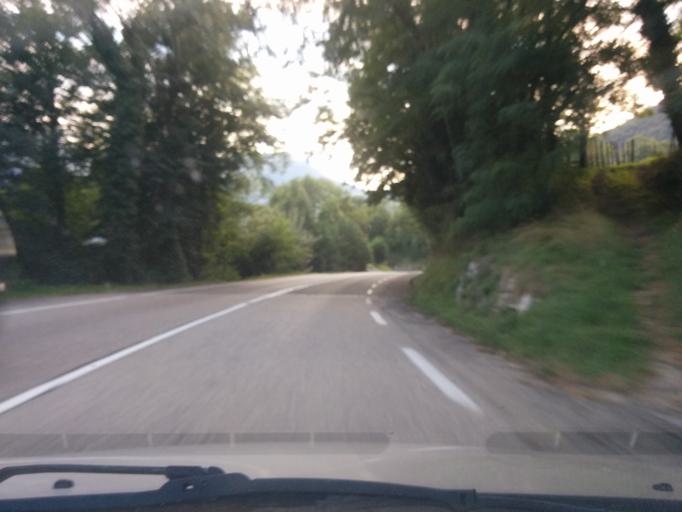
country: FR
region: Rhone-Alpes
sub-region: Departement de l'Isere
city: Voreppe
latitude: 45.3107
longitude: 5.6458
